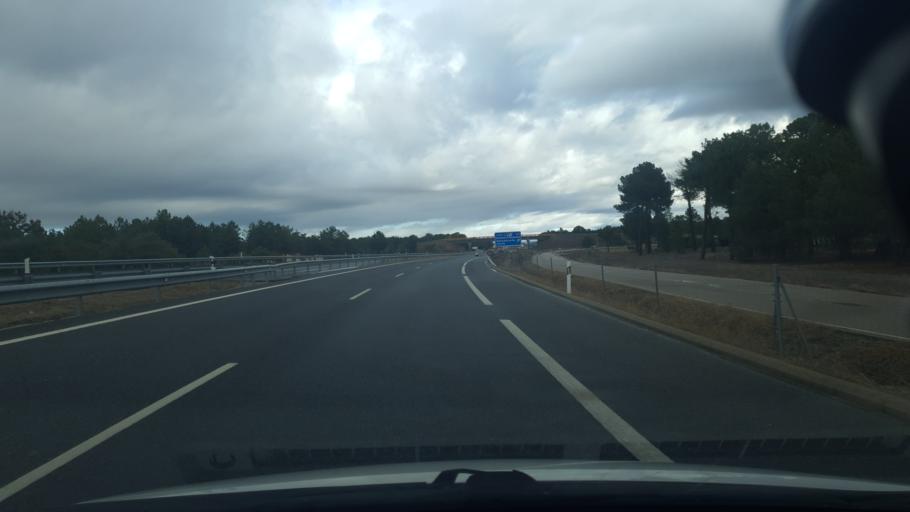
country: ES
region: Castille and Leon
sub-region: Provincia de Segovia
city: Sanchonuno
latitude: 41.3304
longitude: -4.3121
